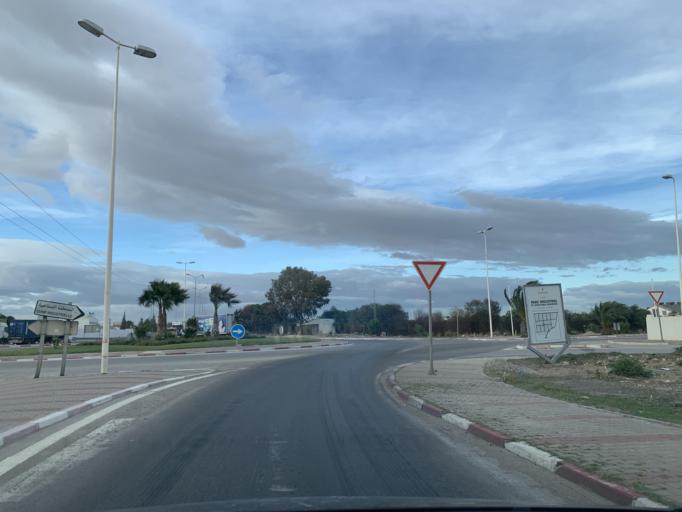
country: TN
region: Susah
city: Harqalah
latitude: 36.1103
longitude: 10.3861
